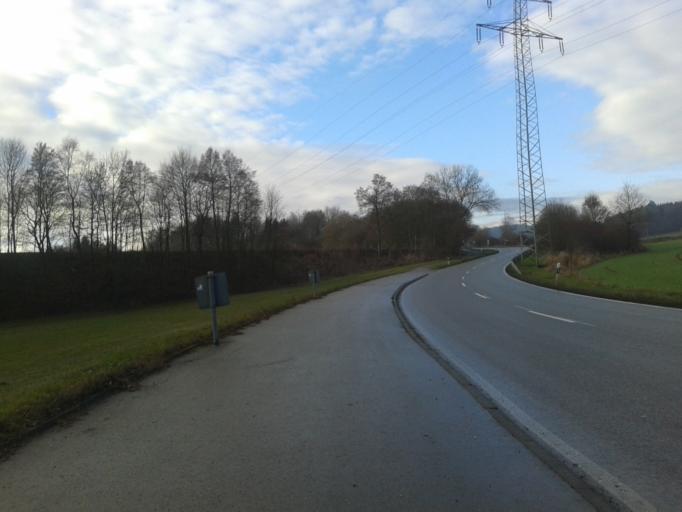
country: DE
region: Baden-Wuerttemberg
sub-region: Tuebingen Region
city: Ulm
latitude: 48.3959
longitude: 9.9281
